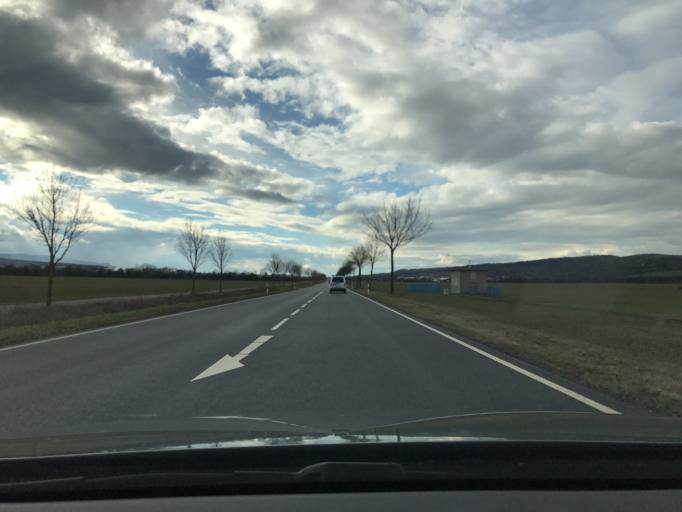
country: DE
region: Saxony-Anhalt
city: Wallhausen
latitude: 51.4599
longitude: 11.2317
